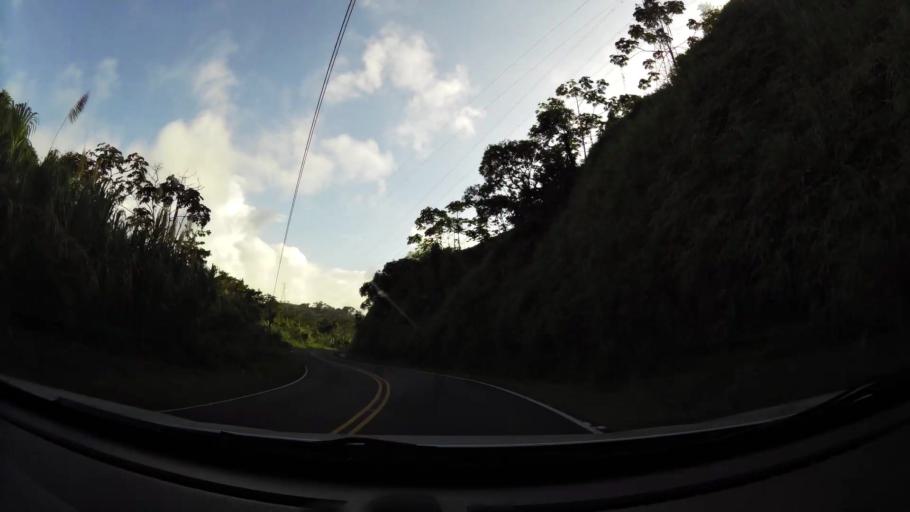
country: CR
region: Limon
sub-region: Canton de Siquirres
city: Siquirres
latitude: 10.0458
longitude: -83.5485
